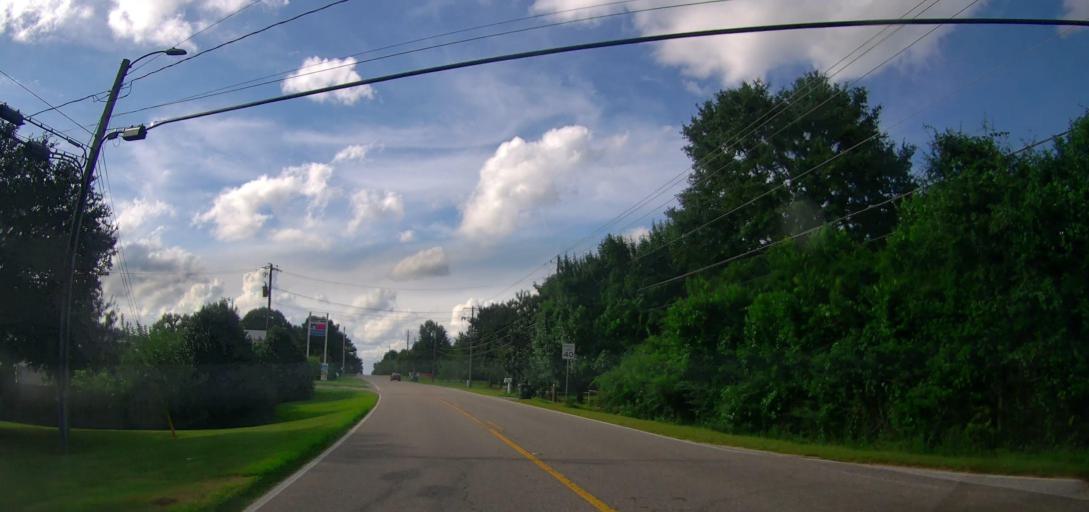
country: US
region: Alabama
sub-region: Russell County
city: Phenix City
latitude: 32.5114
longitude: -85.0208
